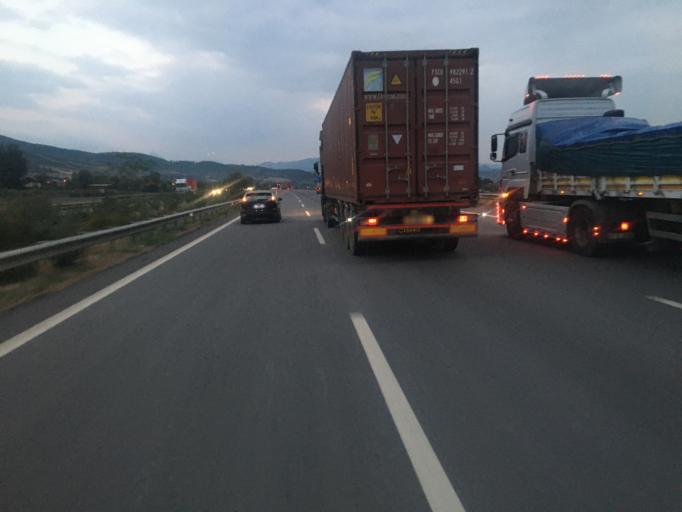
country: TR
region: Osmaniye
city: Osmaniye
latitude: 37.1343
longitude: 36.3107
